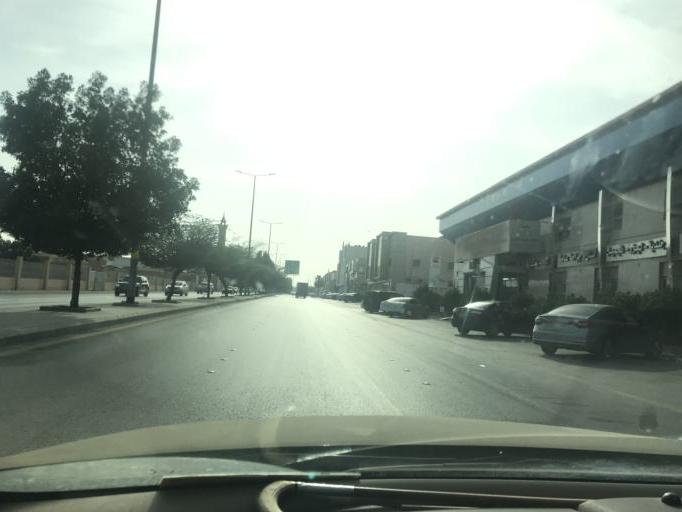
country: SA
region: Ar Riyad
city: Riyadh
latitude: 24.7310
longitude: 46.7711
